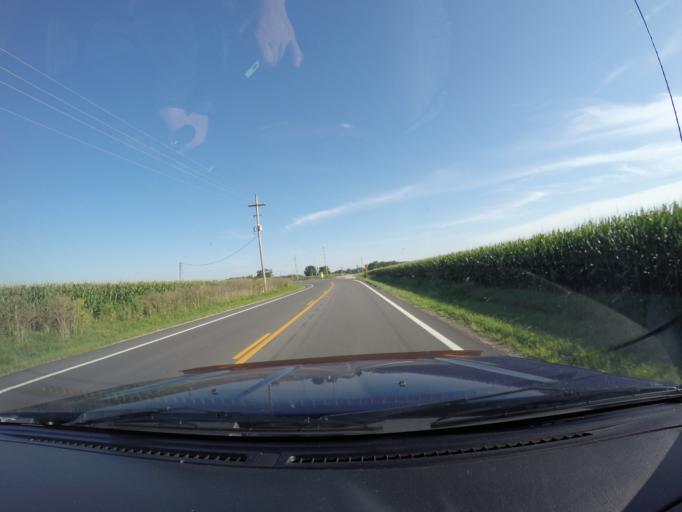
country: US
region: Kansas
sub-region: Douglas County
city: Lawrence
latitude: 39.0558
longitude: -95.2982
